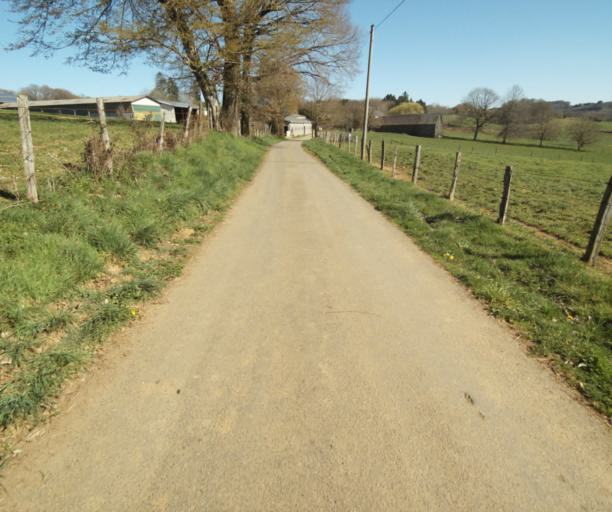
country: FR
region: Limousin
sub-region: Departement de la Correze
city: Chamboulive
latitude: 45.4154
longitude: 1.6734
